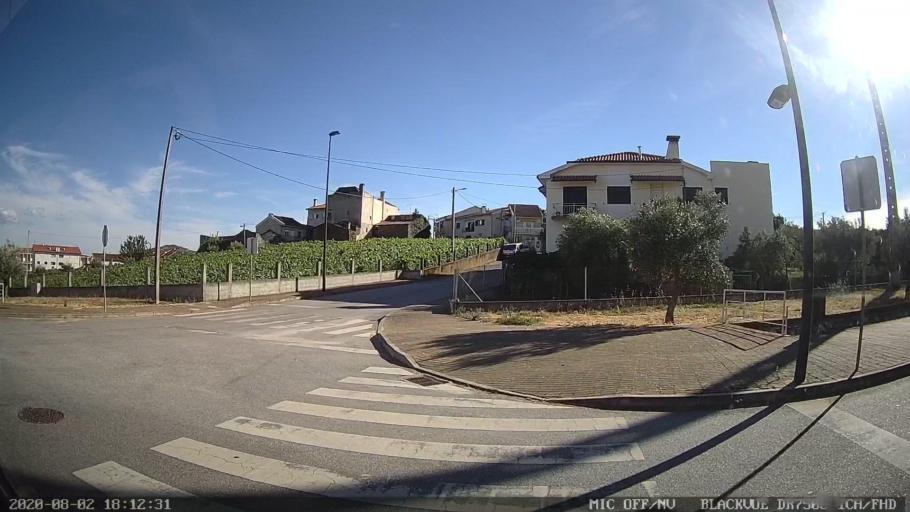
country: PT
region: Vila Real
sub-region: Murca
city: Murca
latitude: 41.4095
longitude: -7.4529
